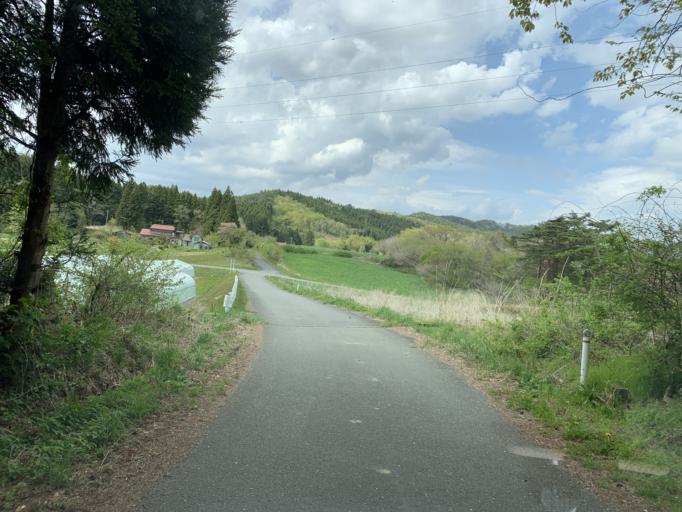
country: JP
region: Iwate
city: Ichinoseki
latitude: 38.7882
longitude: 141.4346
